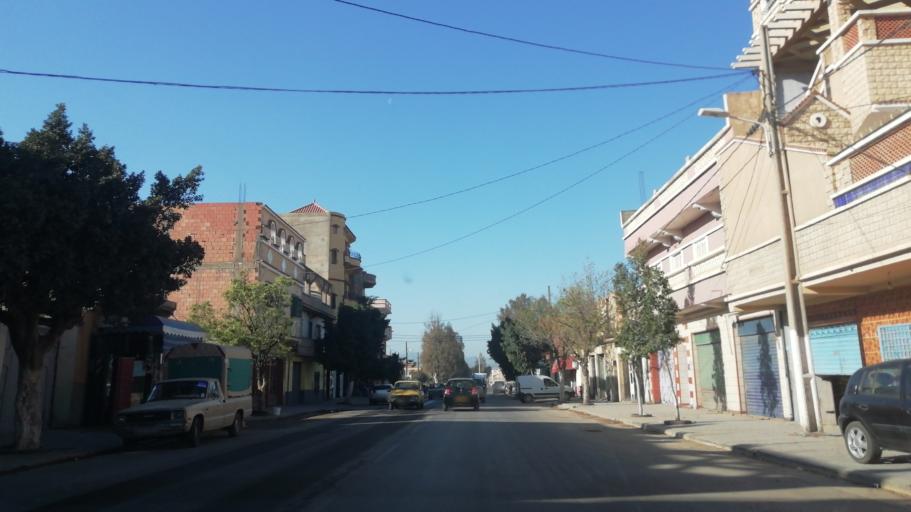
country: DZ
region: Mascara
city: Mascara
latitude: 35.6193
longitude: 0.1115
